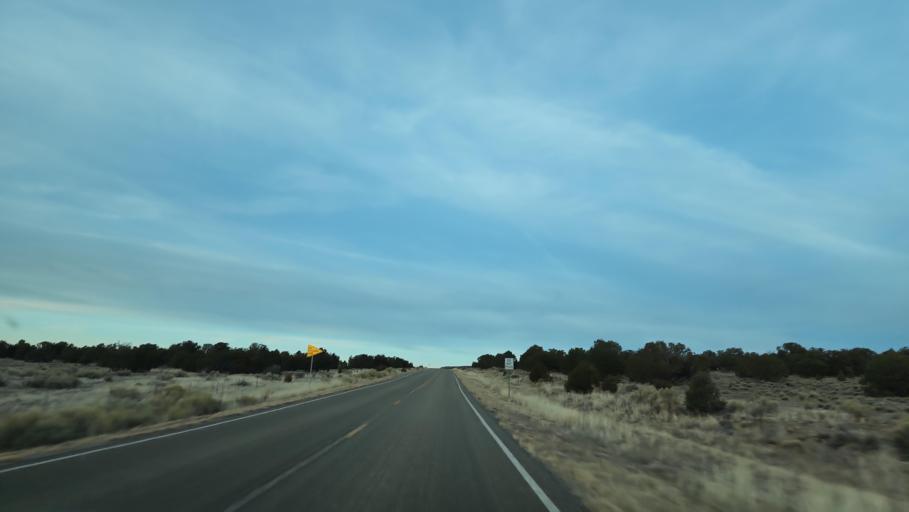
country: US
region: New Mexico
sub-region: Cibola County
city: Grants
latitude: 34.7198
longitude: -107.9808
